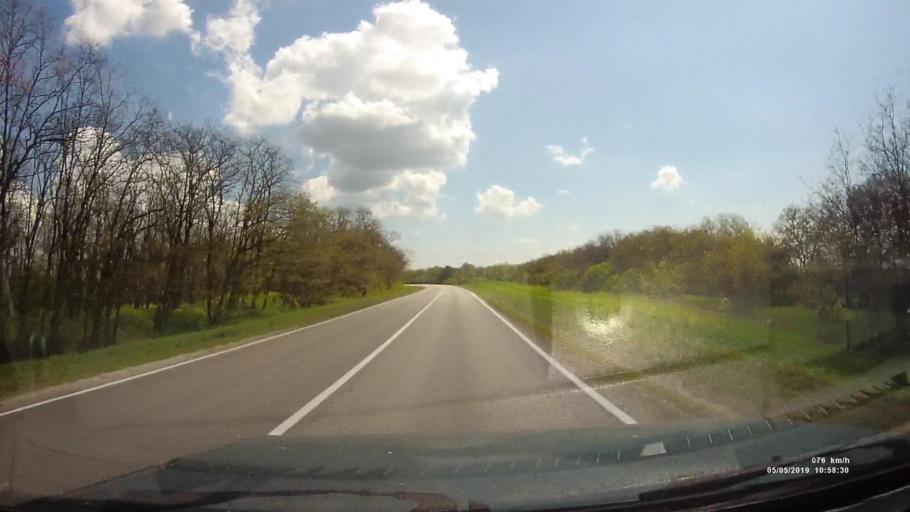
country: RU
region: Rostov
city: Ust'-Donetskiy
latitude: 47.6691
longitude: 40.8540
